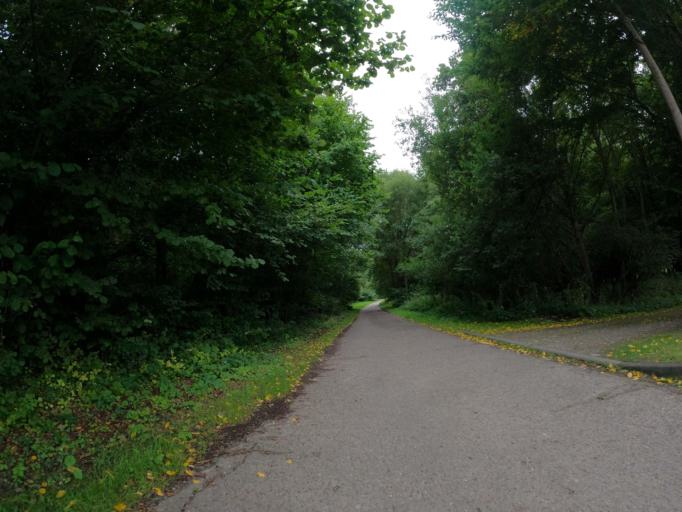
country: DE
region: Mecklenburg-Vorpommern
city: Sehlen
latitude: 54.3600
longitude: 13.4235
